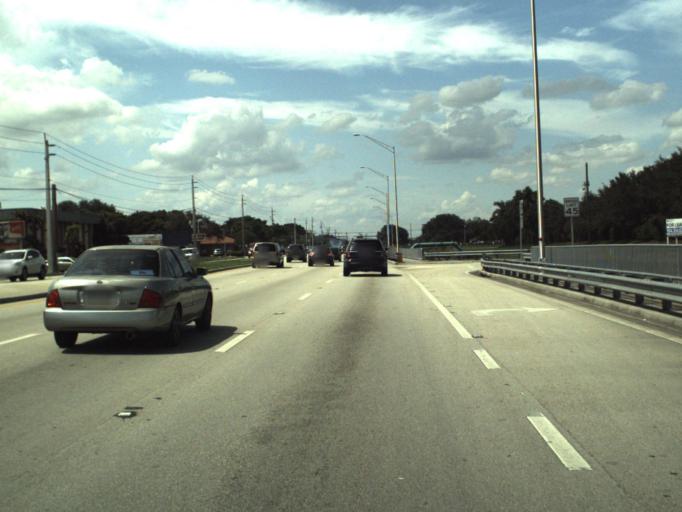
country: US
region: Florida
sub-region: Broward County
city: Pembroke Pines
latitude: 26.0244
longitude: -80.2486
